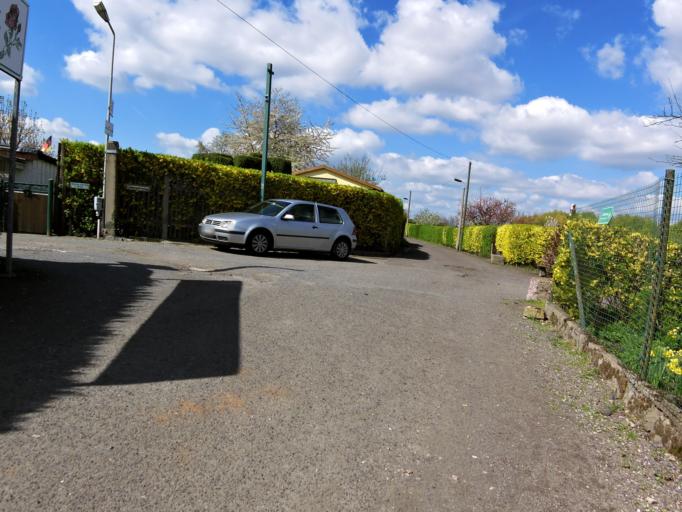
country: DE
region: Saxony
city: Leipzig
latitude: 51.3395
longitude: 12.4255
